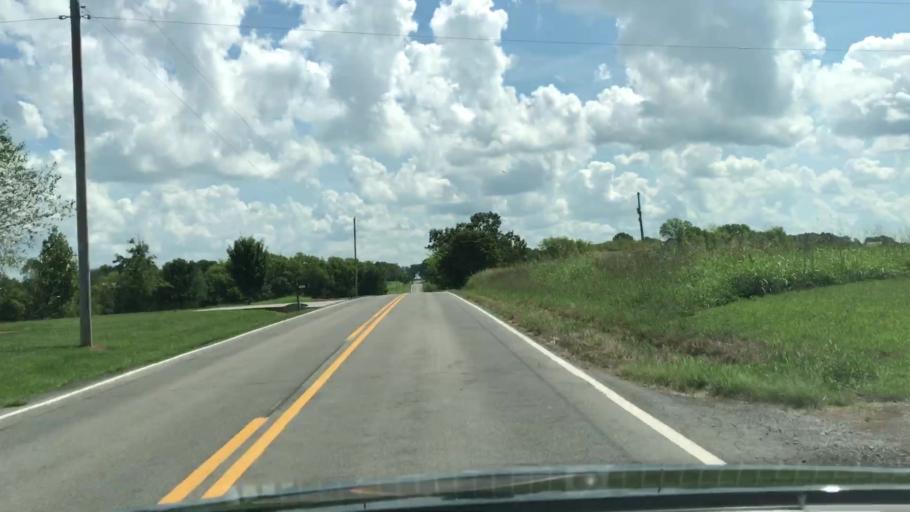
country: US
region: Tennessee
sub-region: Robertson County
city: Springfield
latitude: 36.5961
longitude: -86.9081
